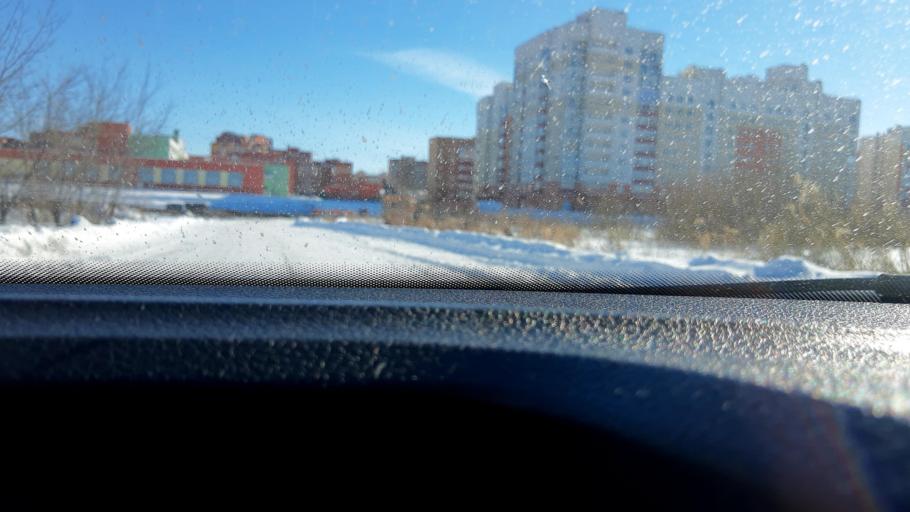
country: RU
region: Bashkortostan
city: Mikhaylovka
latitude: 54.7168
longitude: 55.8366
